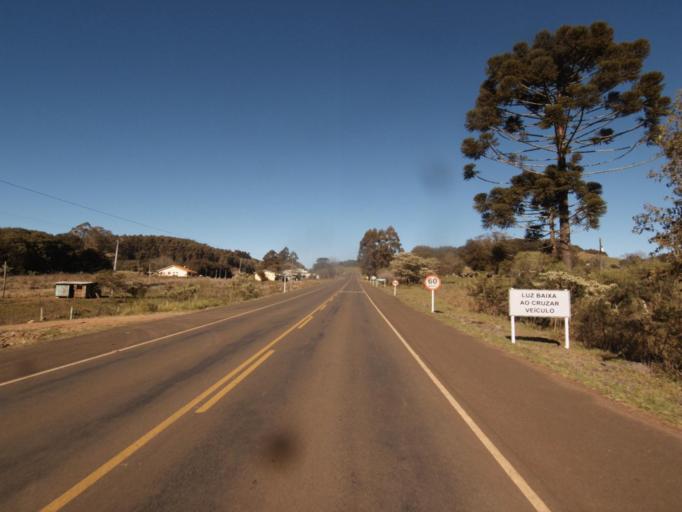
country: AR
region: Misiones
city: Bernardo de Irigoyen
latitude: -26.6765
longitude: -53.5624
